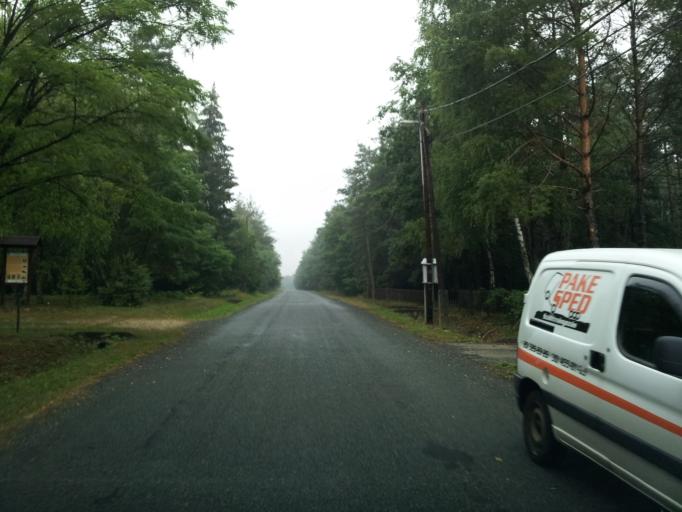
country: HU
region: Zala
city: Zalalovo
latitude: 46.8796
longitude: 16.5488
